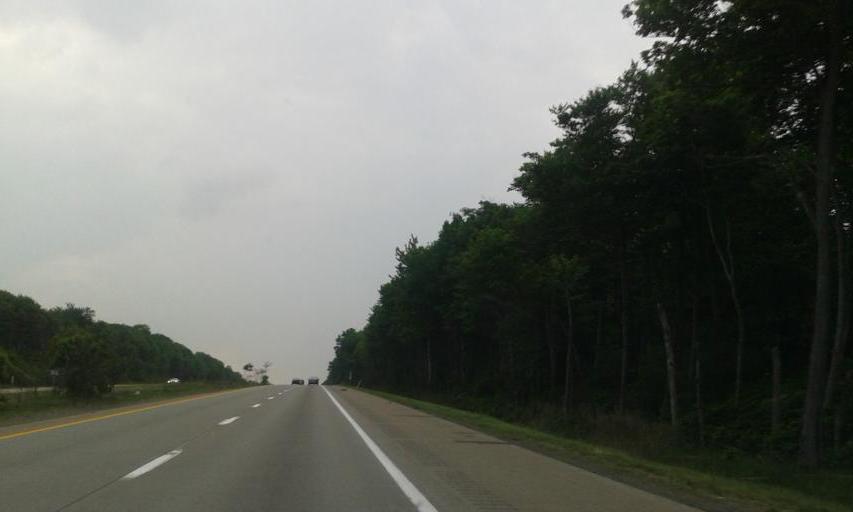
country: US
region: Pennsylvania
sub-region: Monroe County
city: Pocono Pines
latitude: 41.1946
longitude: -75.4477
